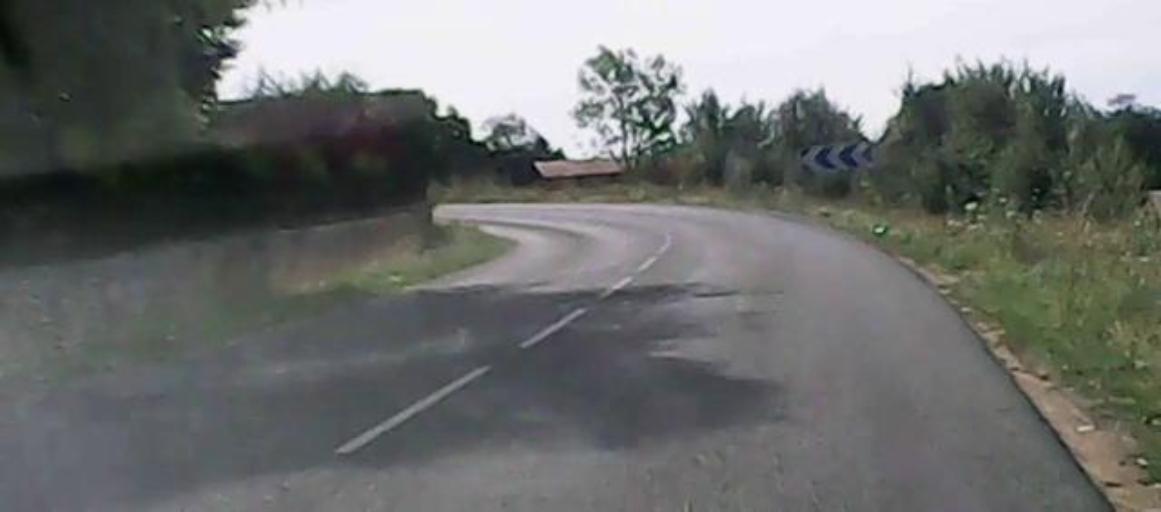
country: FR
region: Auvergne
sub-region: Departement de l'Allier
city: Saint-Yorre
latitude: 46.0625
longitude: 3.5023
